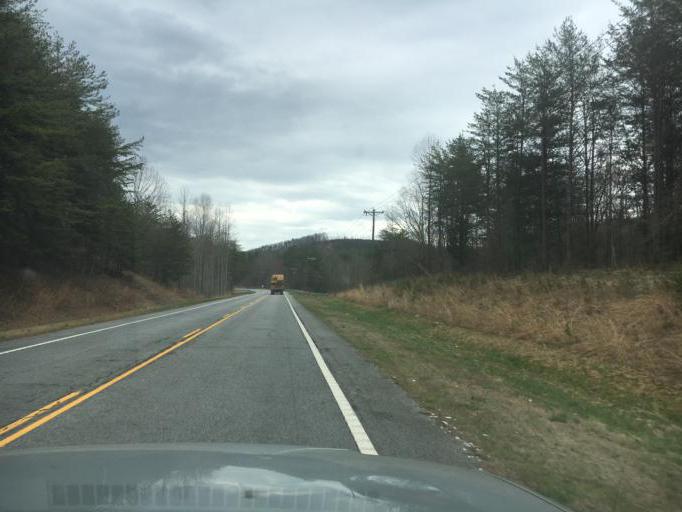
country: US
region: South Carolina
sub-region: Pickens County
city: Pickens
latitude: 34.9814
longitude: -82.7760
